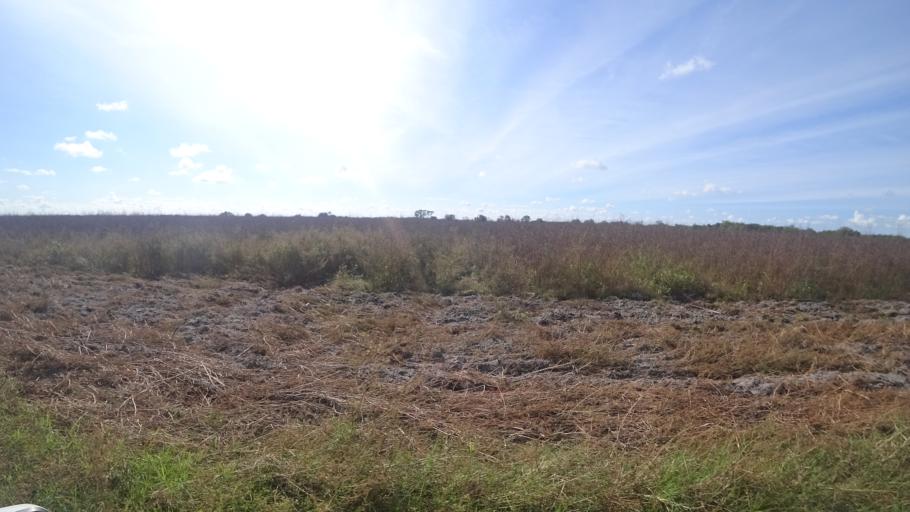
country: US
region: Florida
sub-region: Sarasota County
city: The Meadows
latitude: 27.4521
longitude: -82.3269
